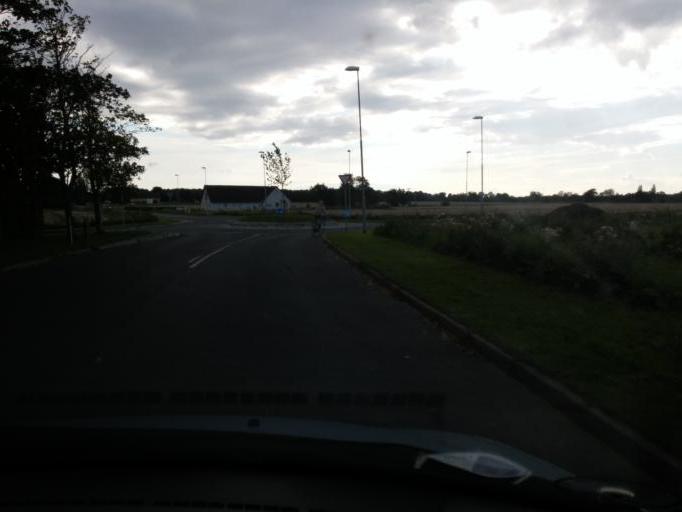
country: DK
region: South Denmark
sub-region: Kerteminde Kommune
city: Munkebo
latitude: 55.4380
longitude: 10.5413
